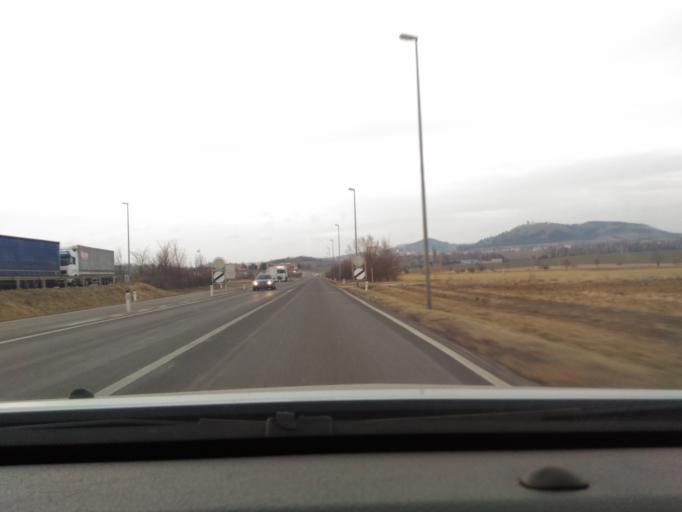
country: CZ
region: South Moravian
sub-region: Okres Breclav
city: Mikulov
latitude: 48.7822
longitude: 16.6395
